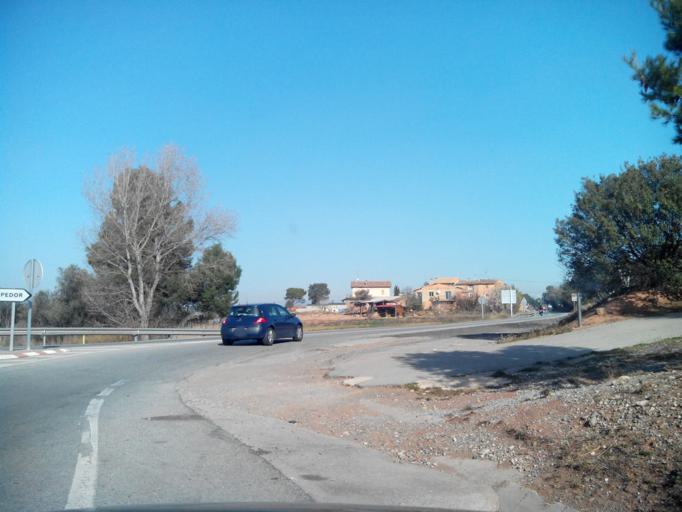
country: ES
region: Catalonia
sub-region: Provincia de Barcelona
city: Sant Fruitos de Bages
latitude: 41.7518
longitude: 1.8413
